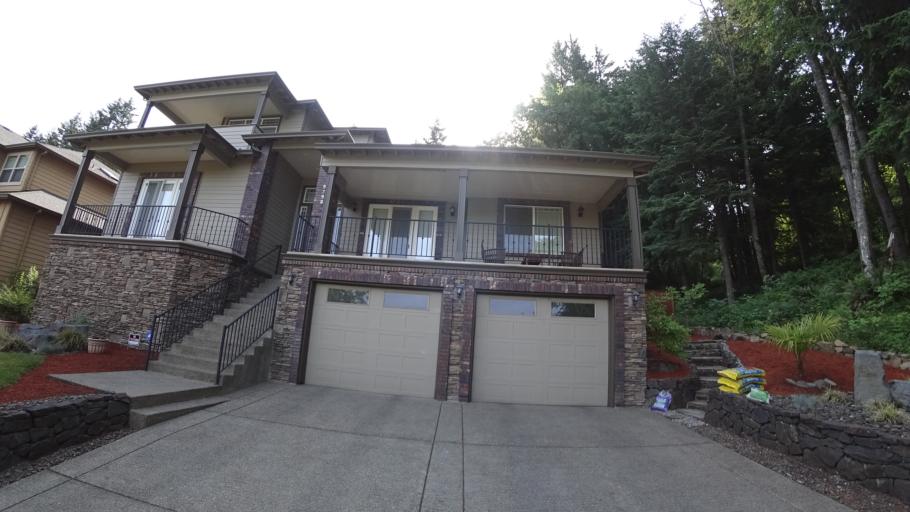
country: US
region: Oregon
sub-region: Clackamas County
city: Happy Valley
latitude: 45.4515
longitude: -122.5111
